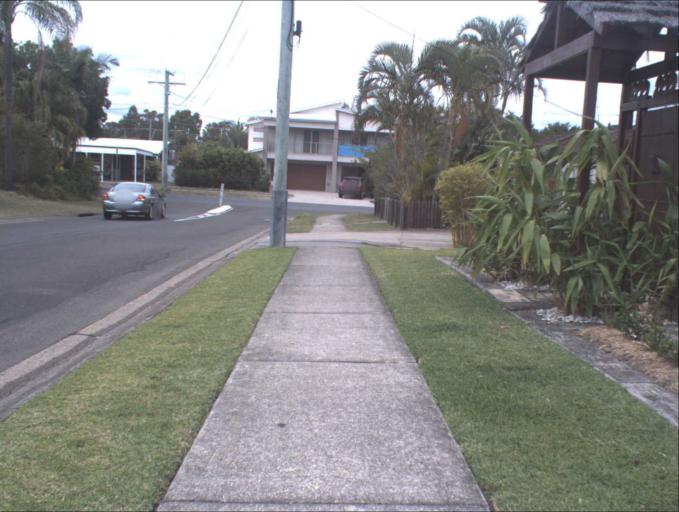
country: AU
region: Queensland
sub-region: Logan
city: Slacks Creek
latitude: -27.6328
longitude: 153.1416
